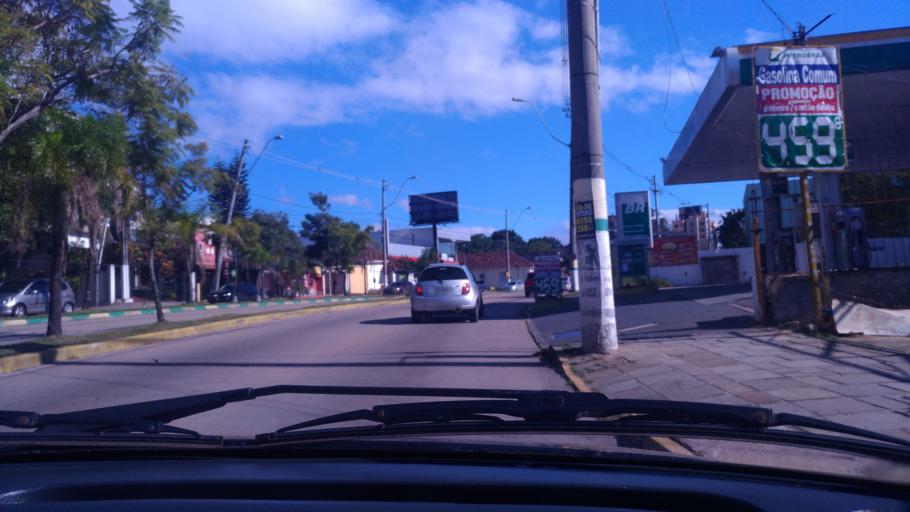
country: BR
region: Rio Grande do Sul
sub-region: Porto Alegre
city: Porto Alegre
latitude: -30.0713
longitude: -51.1901
